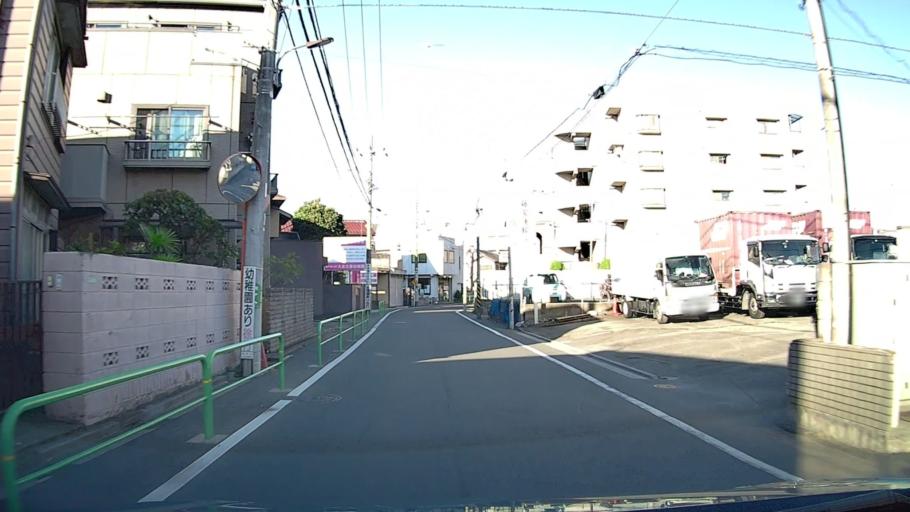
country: JP
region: Saitama
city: Wako
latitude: 35.7551
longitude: 139.5855
